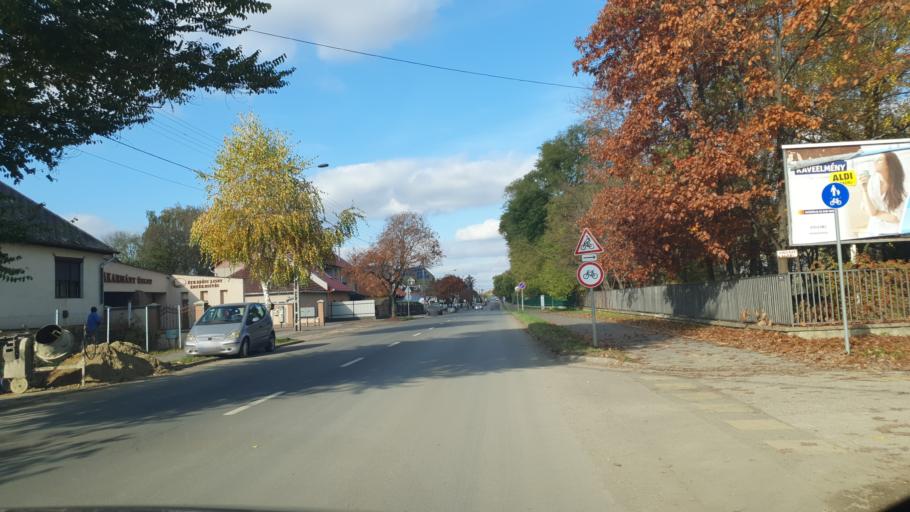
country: HU
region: Szabolcs-Szatmar-Bereg
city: Kisvarda
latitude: 48.2060
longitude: 22.0895
